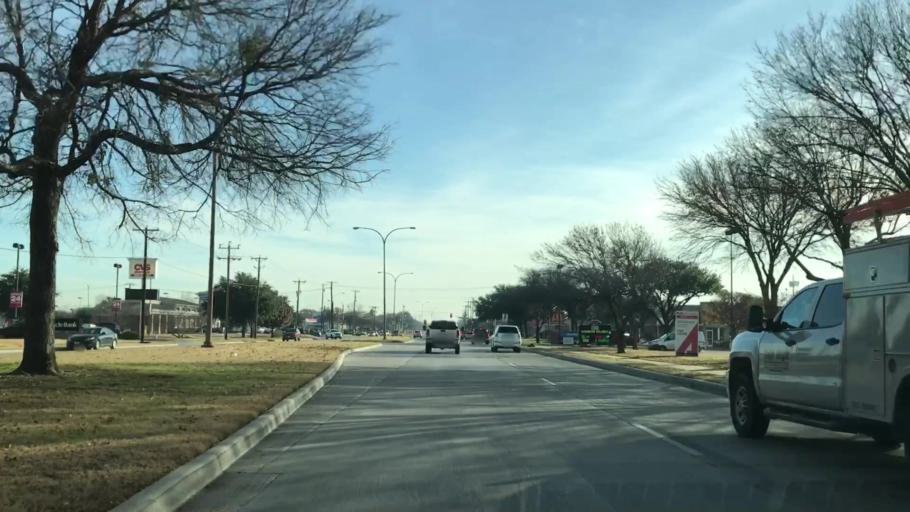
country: US
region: Texas
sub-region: Tarrant County
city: Watauga
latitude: 32.8610
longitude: -97.2925
